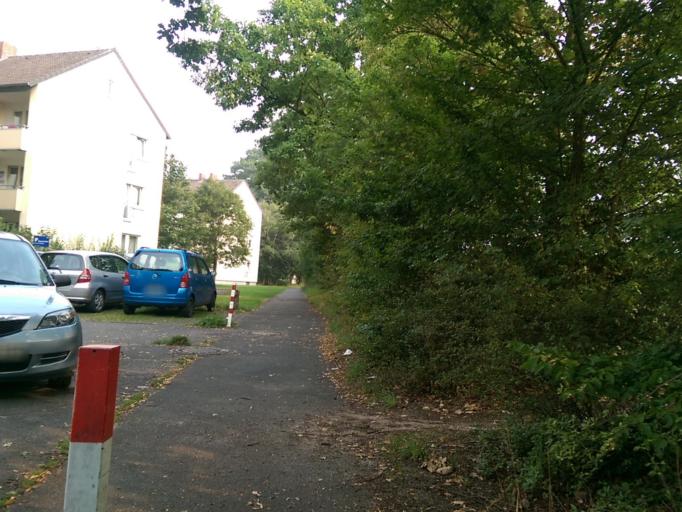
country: DE
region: North Rhine-Westphalia
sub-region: Regierungsbezirk Detmold
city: Guetersloh
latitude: 51.9020
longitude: 8.3595
